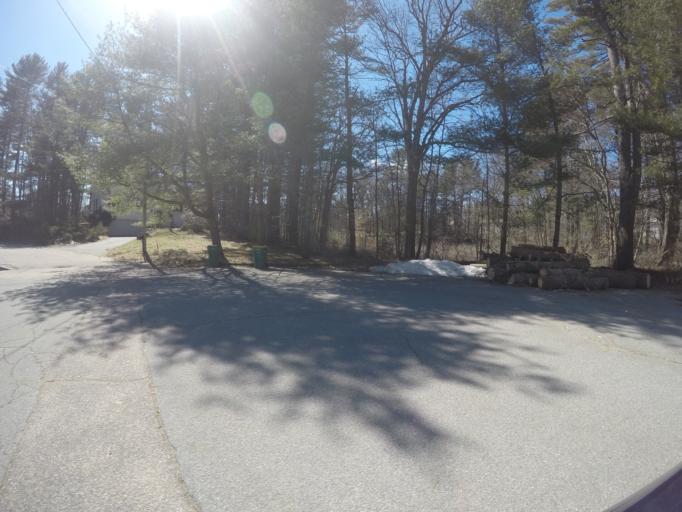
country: US
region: Massachusetts
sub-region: Bristol County
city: Easton
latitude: 42.0156
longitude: -71.1591
